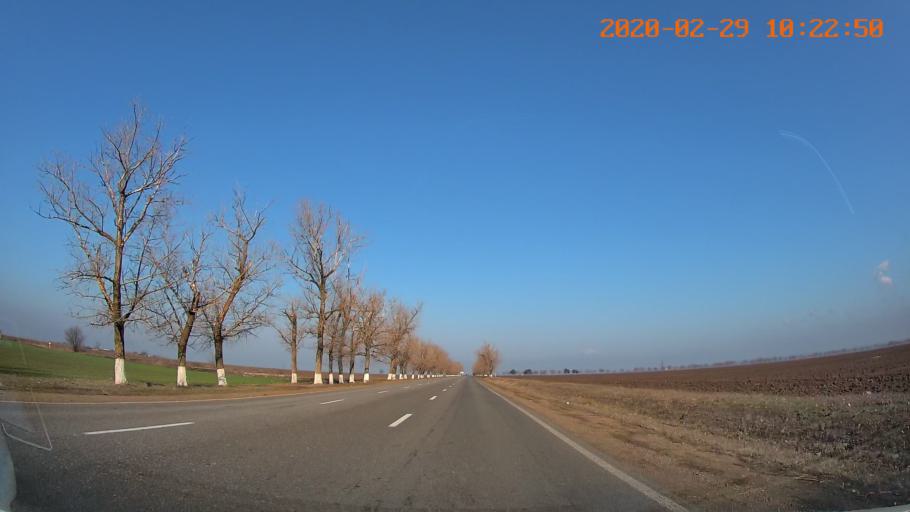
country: MD
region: Telenesti
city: Tiraspolul Nou
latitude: 46.8798
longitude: 29.6051
